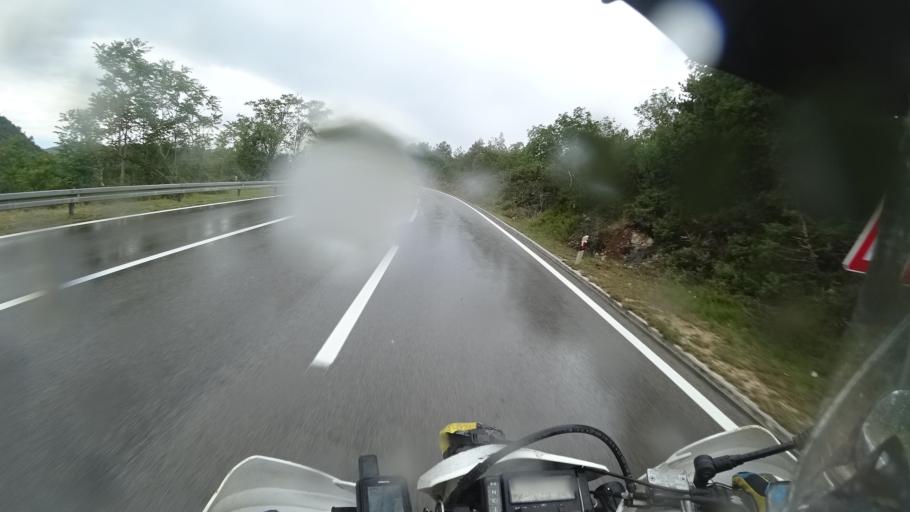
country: HR
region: Sibensko-Kniniska
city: Knin
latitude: 44.0432
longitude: 16.1862
